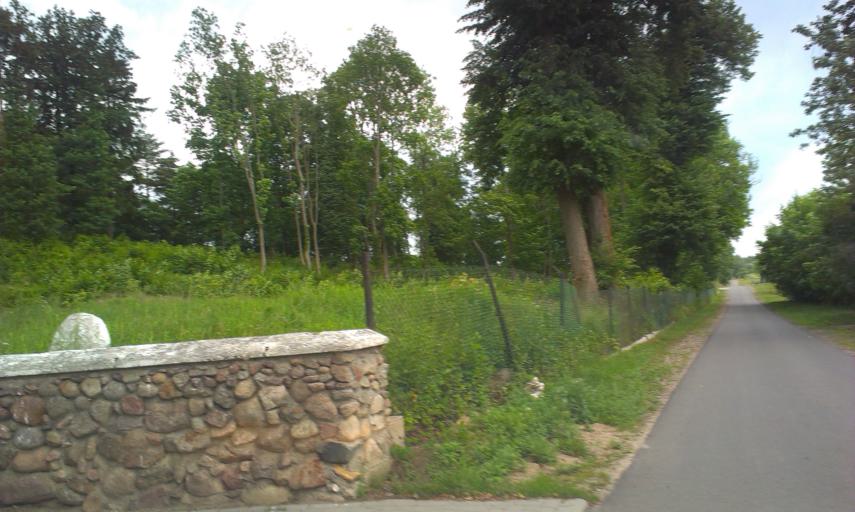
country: PL
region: West Pomeranian Voivodeship
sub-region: Powiat koszalinski
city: Bobolice
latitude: 53.8588
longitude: 16.6129
